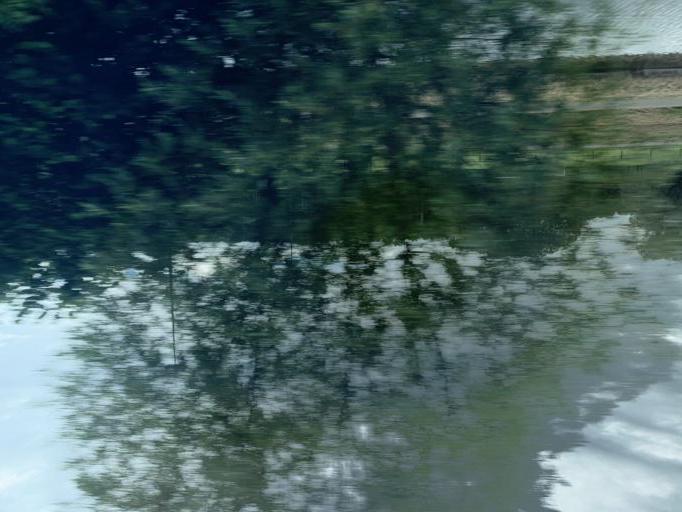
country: FR
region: Alsace
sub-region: Departement du Haut-Rhin
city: Brunstatt
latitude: 47.7223
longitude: 7.3158
